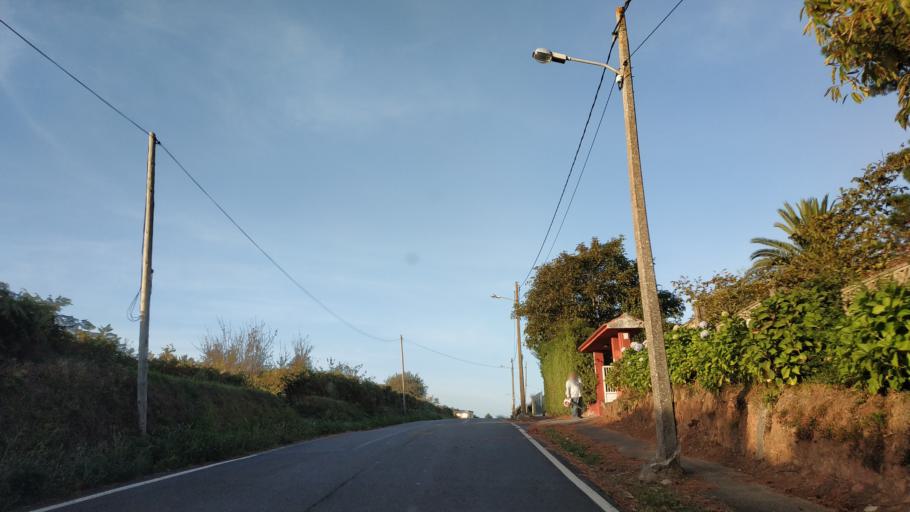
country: ES
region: Galicia
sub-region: Provincia da Coruna
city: Oleiros
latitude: 43.3578
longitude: -8.3440
